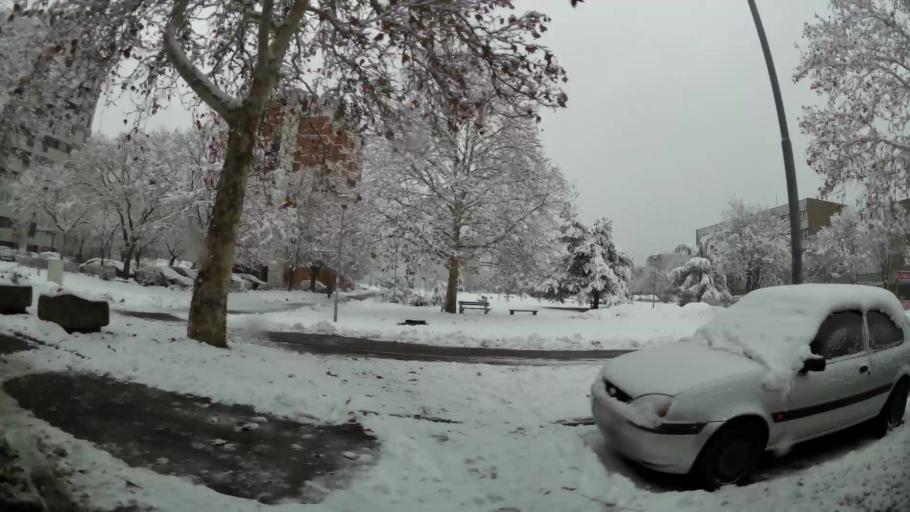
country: RS
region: Central Serbia
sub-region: Belgrade
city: Novi Beograd
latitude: 44.7998
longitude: 20.3893
